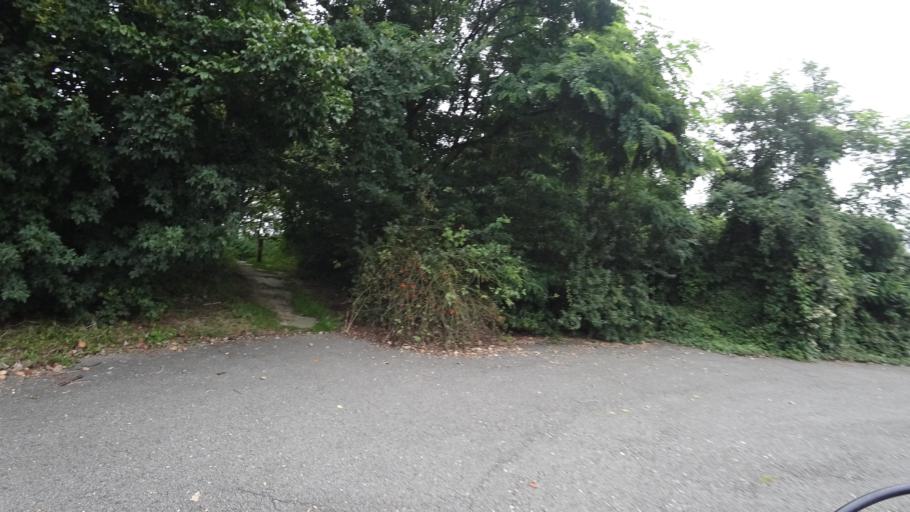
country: BE
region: Wallonia
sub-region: Province du Brabant Wallon
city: Mont-Saint-Guibert
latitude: 50.6366
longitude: 4.6243
